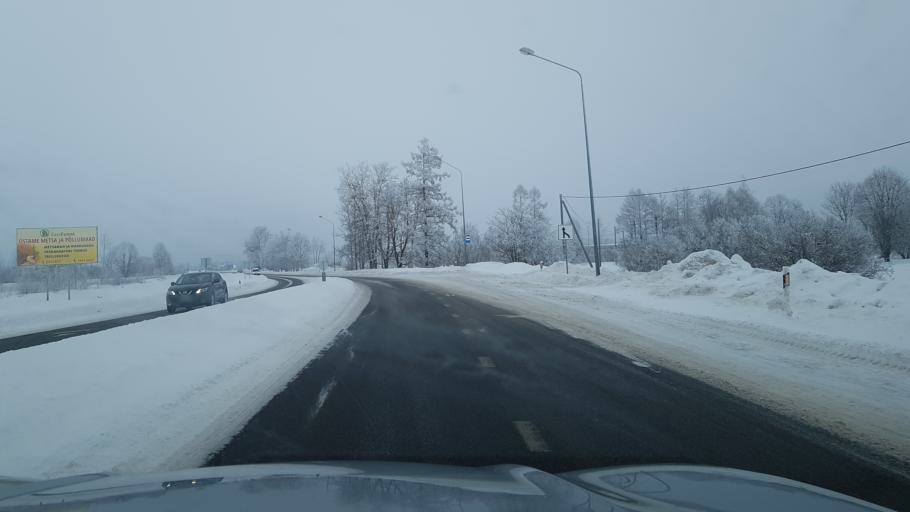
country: EE
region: Ida-Virumaa
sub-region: Johvi vald
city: Johvi
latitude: 59.3301
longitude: 27.4023
